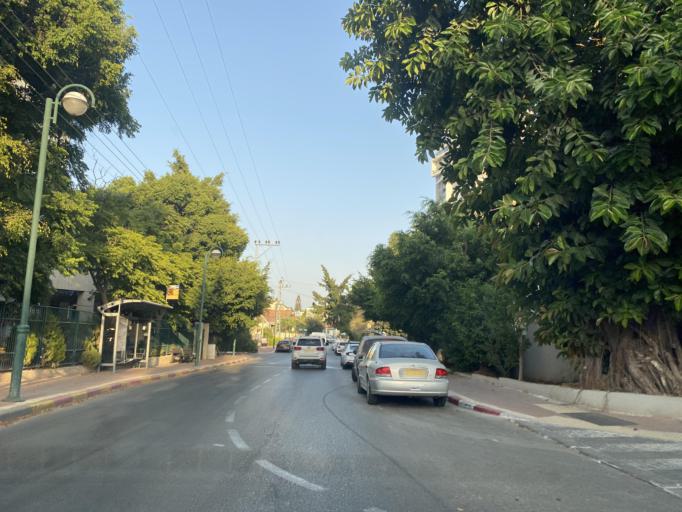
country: IL
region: Tel Aviv
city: Ramat HaSharon
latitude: 32.1341
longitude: 34.8577
